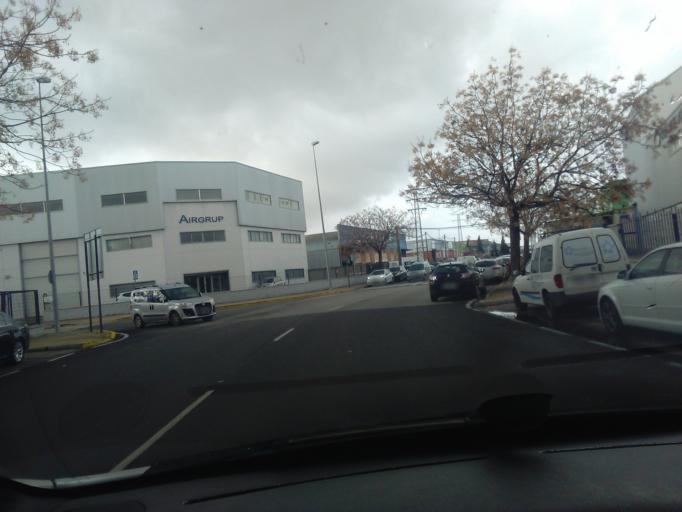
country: ES
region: Andalusia
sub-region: Provincia de Sevilla
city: Sevilla
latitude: 37.3766
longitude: -5.9234
